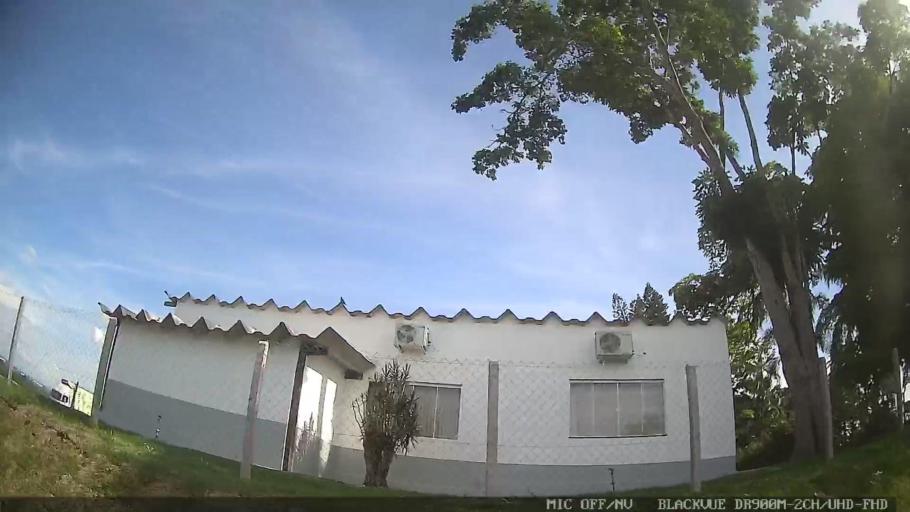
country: BR
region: Sao Paulo
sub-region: Jaguariuna
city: Jaguariuna
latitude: -22.6731
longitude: -47.0807
